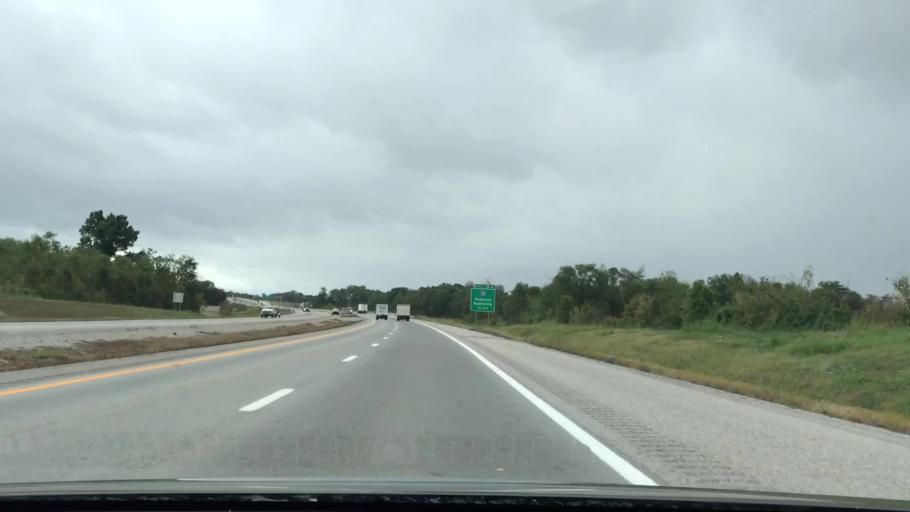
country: US
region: Kentucky
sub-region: Christian County
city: Hopkinsville
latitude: 36.7569
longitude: -87.5062
